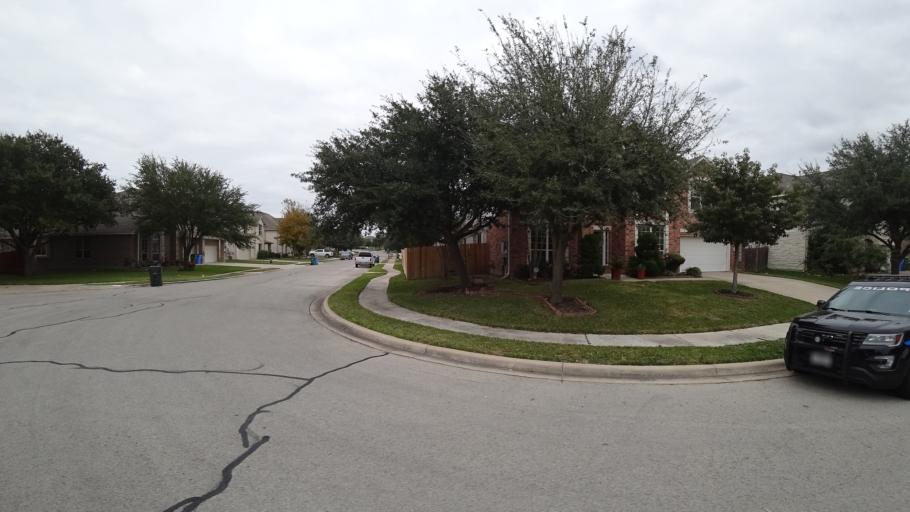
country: US
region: Texas
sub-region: Travis County
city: Pflugerville
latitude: 30.4514
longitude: -97.6249
